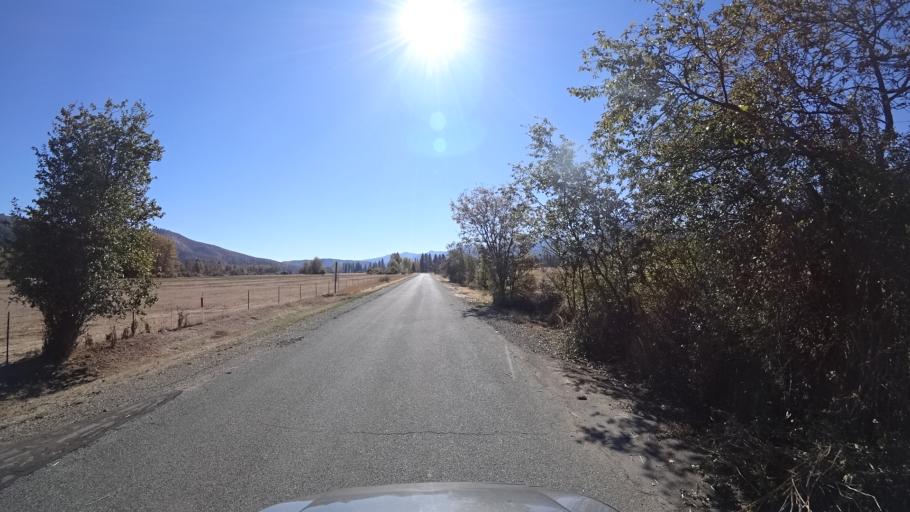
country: US
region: California
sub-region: Siskiyou County
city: Yreka
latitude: 41.6164
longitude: -122.9704
